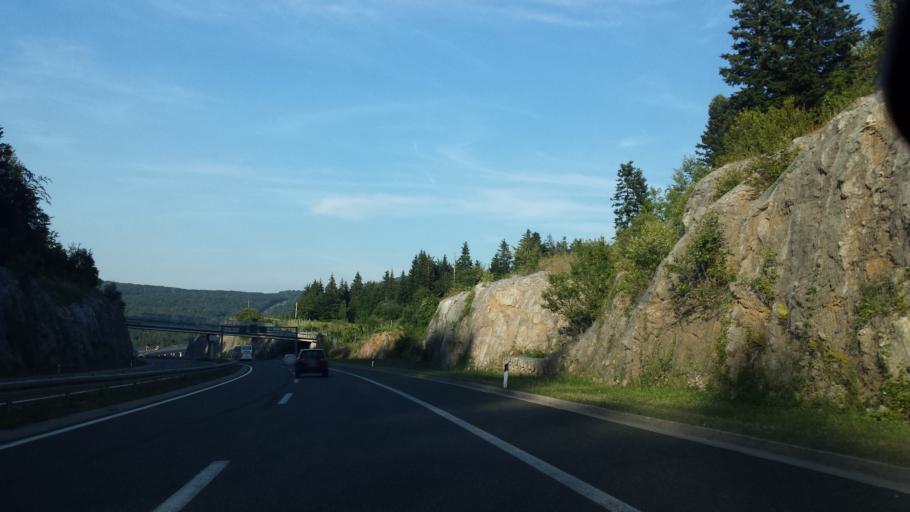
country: HR
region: Primorsko-Goranska
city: Vrbovsko
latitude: 45.3726
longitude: 15.1166
